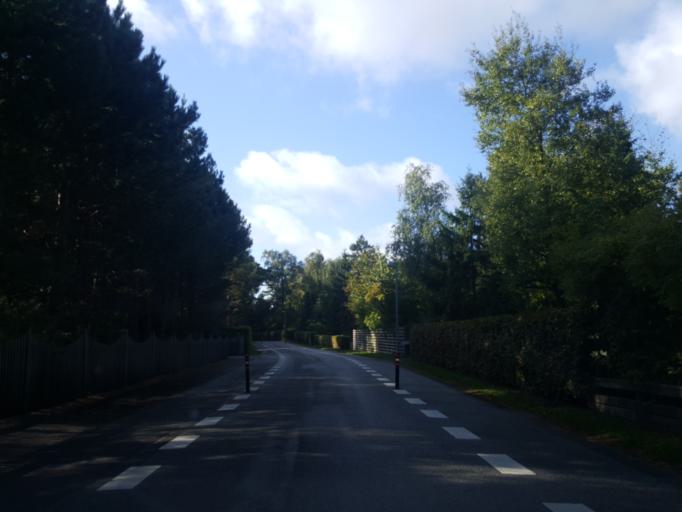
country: DK
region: Zealand
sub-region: Guldborgsund Kommune
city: Nykobing Falster
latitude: 54.6882
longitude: 11.9652
